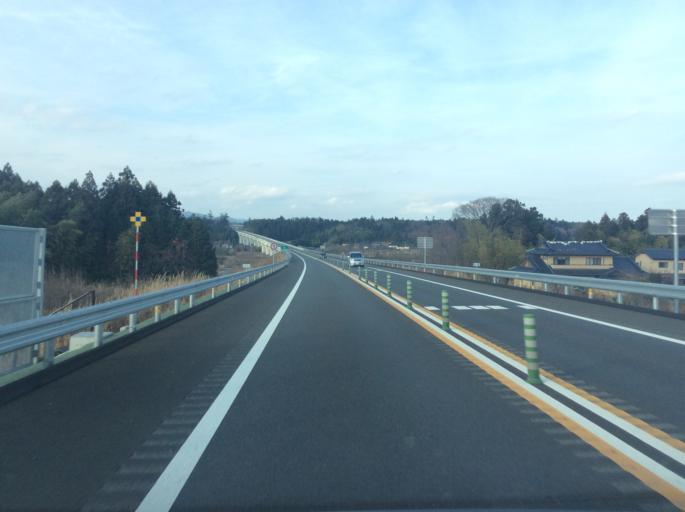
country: JP
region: Fukushima
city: Namie
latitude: 37.4715
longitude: 140.9615
